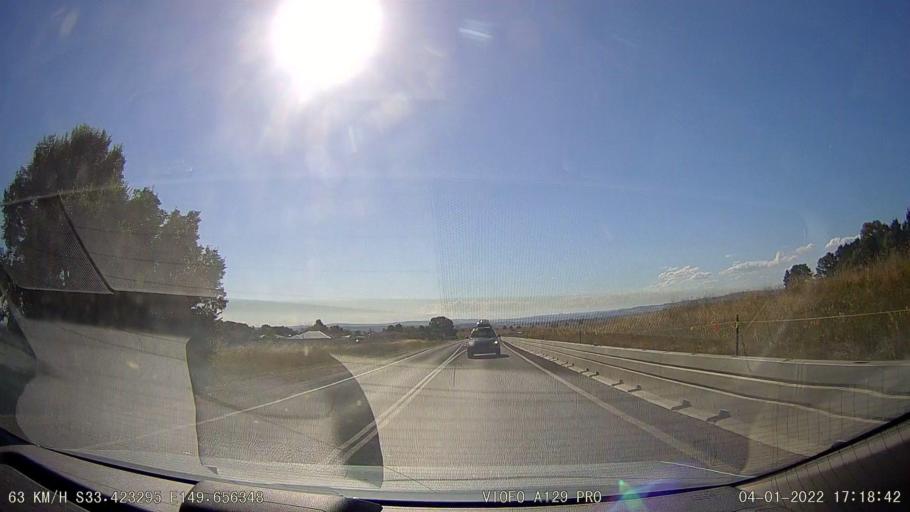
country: AU
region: New South Wales
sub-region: Bathurst Regional
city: Kelso
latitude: -33.4236
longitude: 149.6563
